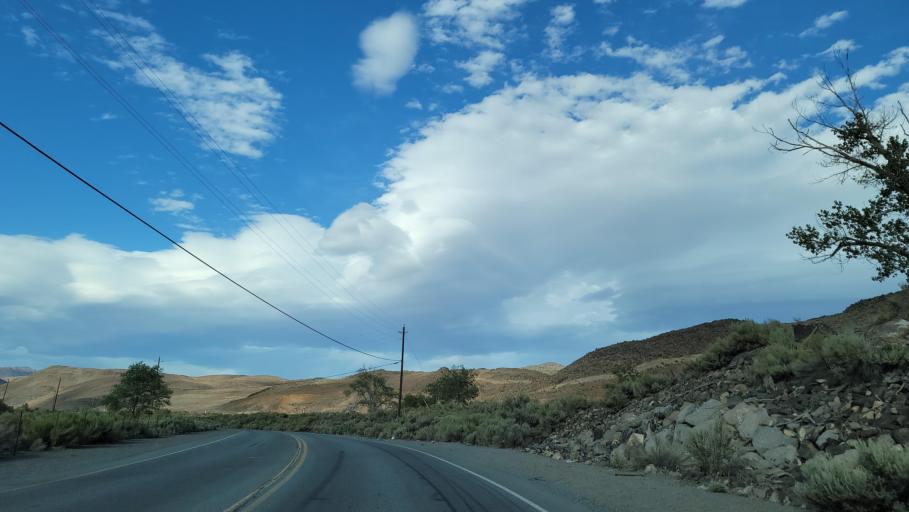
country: US
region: Nevada
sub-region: Washoe County
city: Sparks
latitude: 39.5182
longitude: -119.6137
